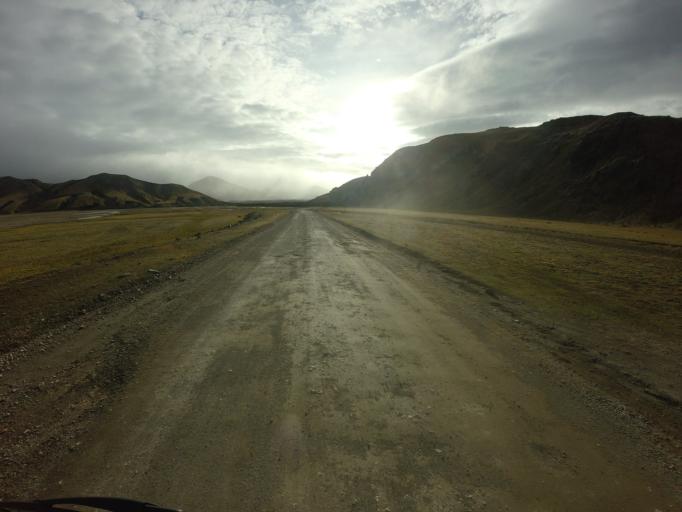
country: IS
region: South
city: Vestmannaeyjar
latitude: 64.0047
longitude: -19.0366
